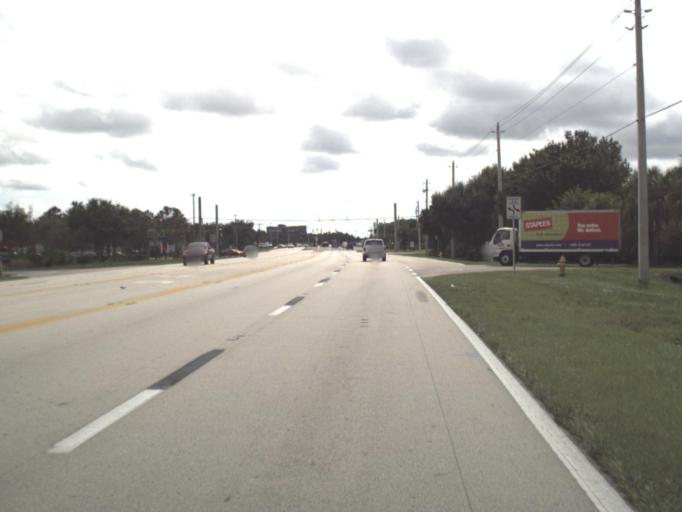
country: US
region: Florida
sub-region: Lee County
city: Villas
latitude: 26.5502
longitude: -81.8529
